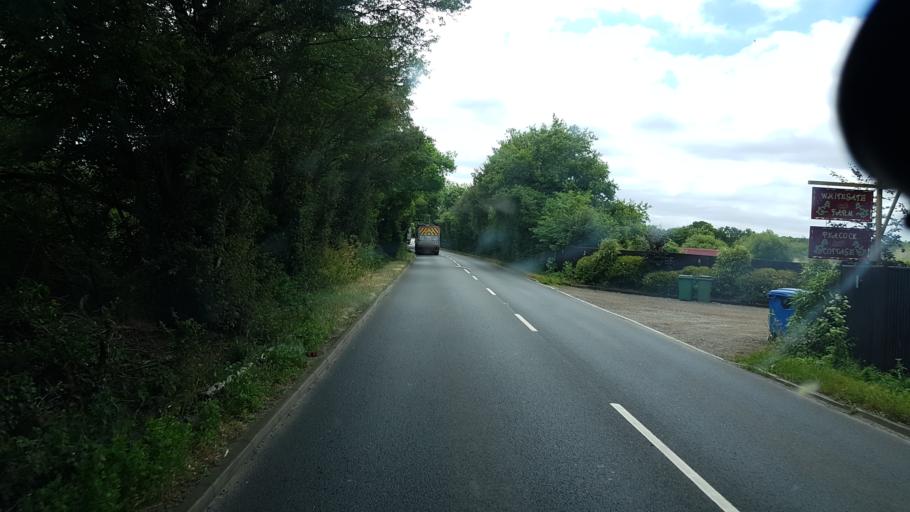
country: GB
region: England
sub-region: Surrey
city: Lingfield
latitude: 51.1817
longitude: -0.0470
